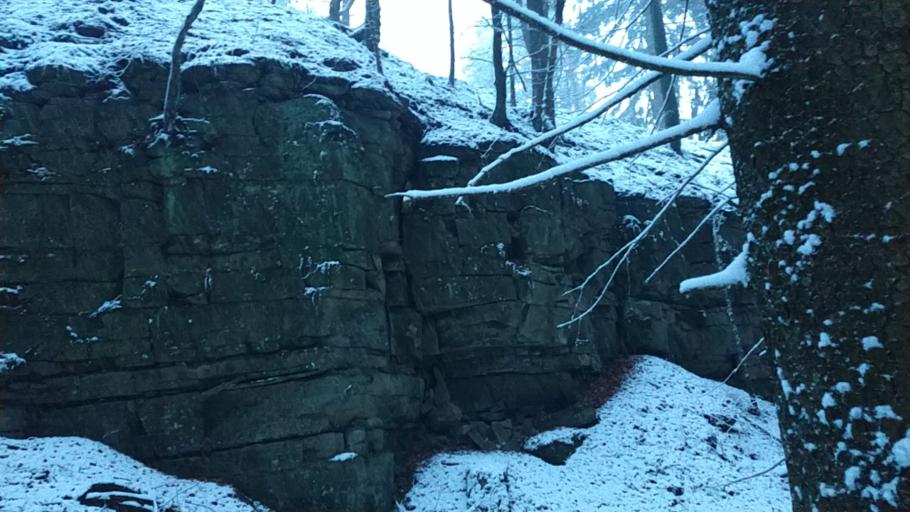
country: DE
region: Lower Saxony
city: Rehren
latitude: 52.2620
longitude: 9.2146
